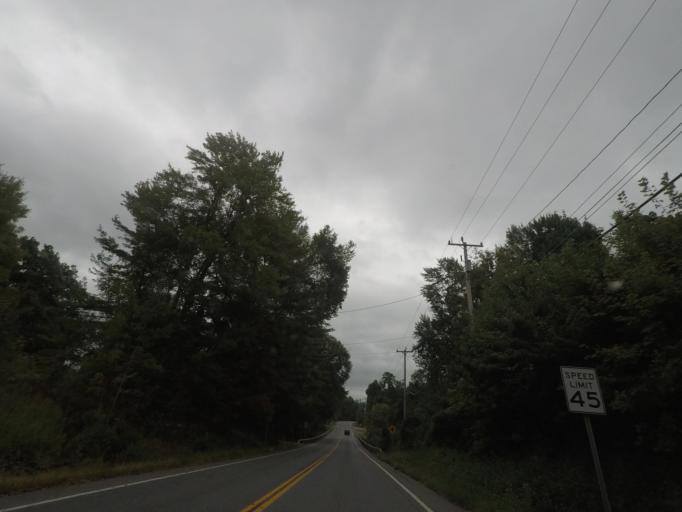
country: US
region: New York
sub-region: Saratoga County
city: Country Knolls
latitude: 42.9463
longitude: -73.7837
